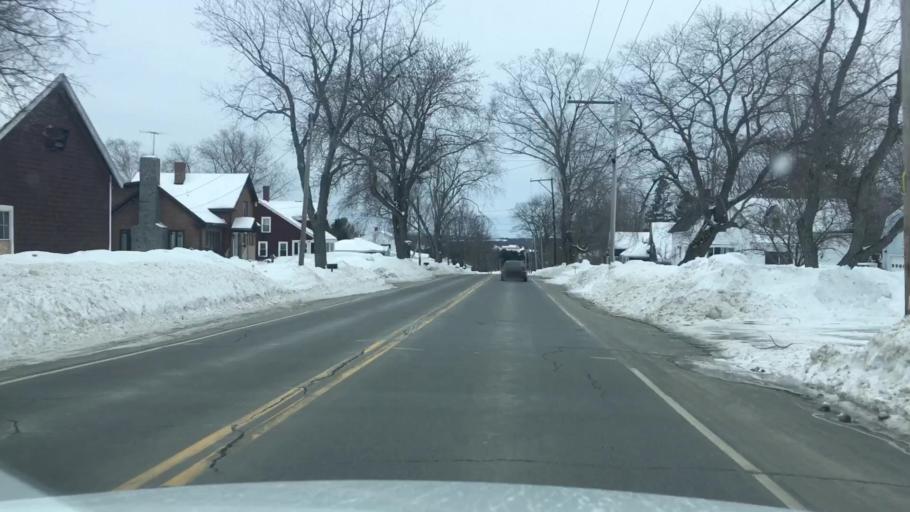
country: US
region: Maine
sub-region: Penobscot County
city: Charleston
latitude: 45.0017
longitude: -69.0279
